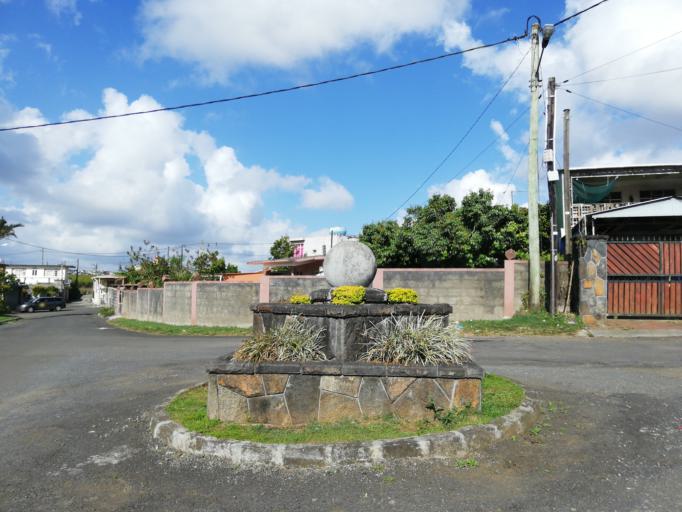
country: MU
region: Moka
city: Verdun
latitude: -20.2232
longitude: 57.5457
